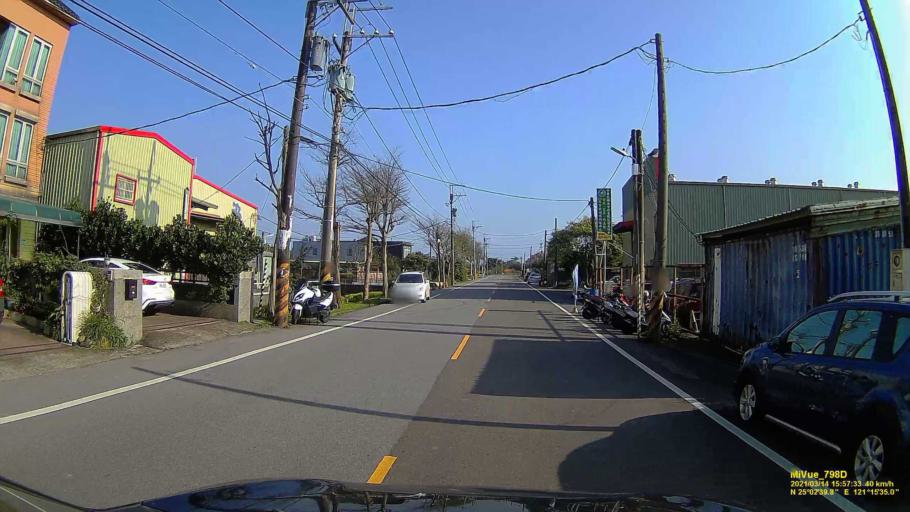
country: TW
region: Taiwan
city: Taoyuan City
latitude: 25.0441
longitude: 121.2598
